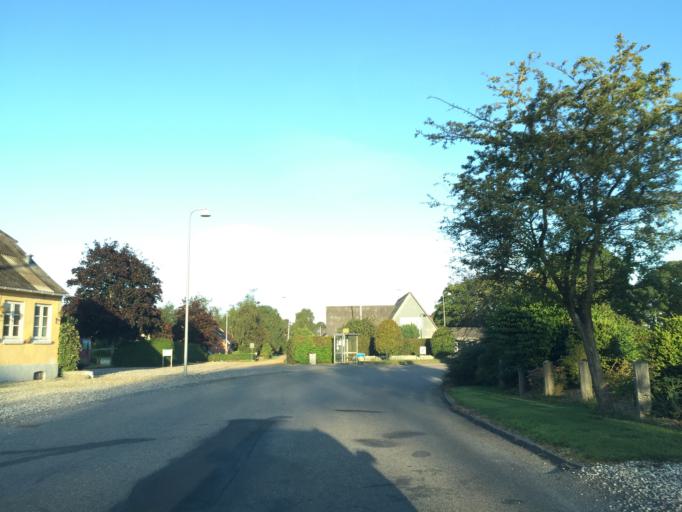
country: DK
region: Central Jutland
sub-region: Viborg Kommune
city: Bjerringbro
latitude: 56.2875
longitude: 9.6793
